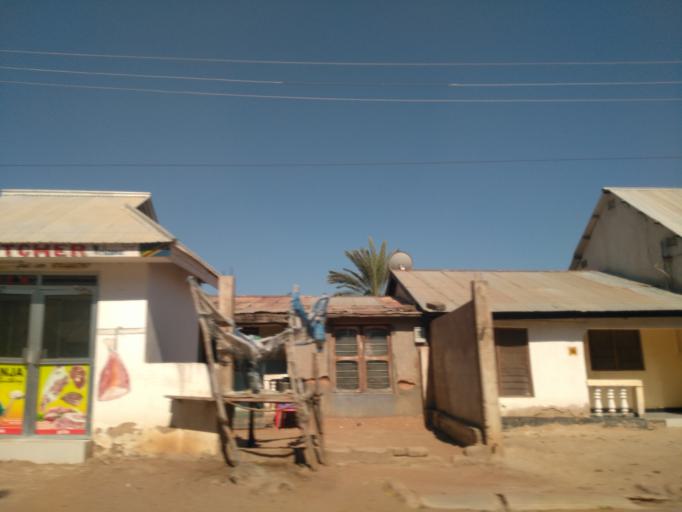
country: TZ
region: Dodoma
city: Dodoma
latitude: -6.1624
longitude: 35.7491
